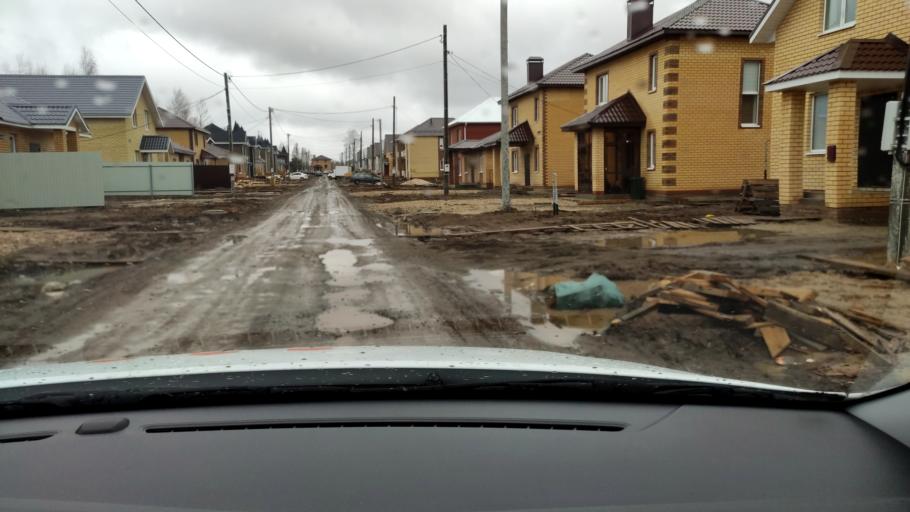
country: RU
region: Tatarstan
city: Stolbishchi
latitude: 55.7193
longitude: 49.3027
